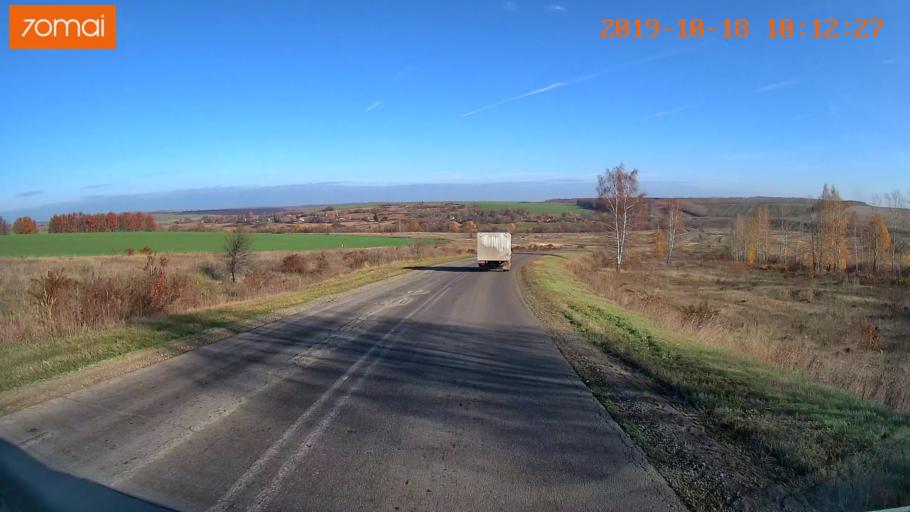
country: RU
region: Tula
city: Kurkino
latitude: 53.3940
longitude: 38.5076
